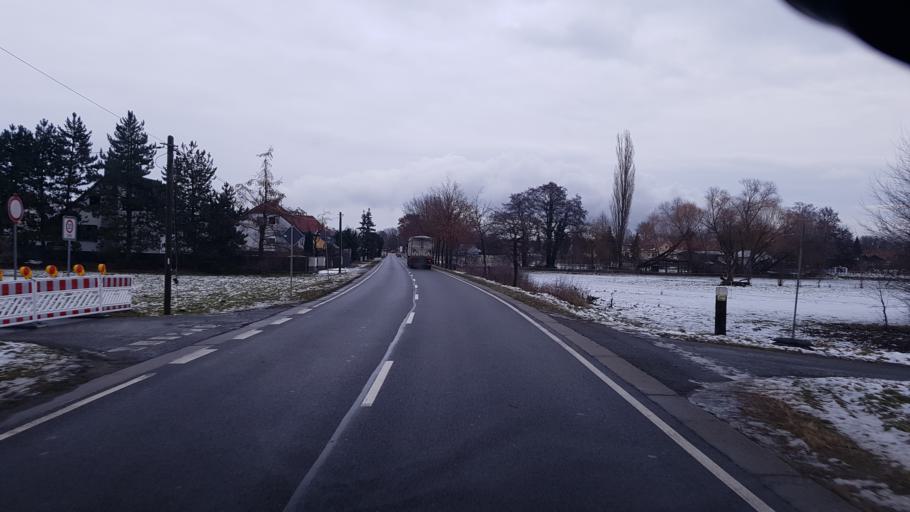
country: DE
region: Brandenburg
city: Peitz
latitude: 51.8496
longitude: 14.4170
